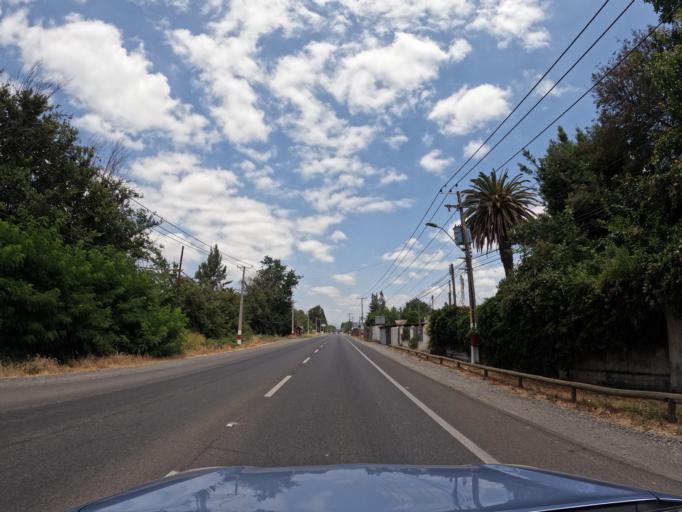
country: CL
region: Maule
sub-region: Provincia de Curico
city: Curico
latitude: -35.0042
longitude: -71.2252
